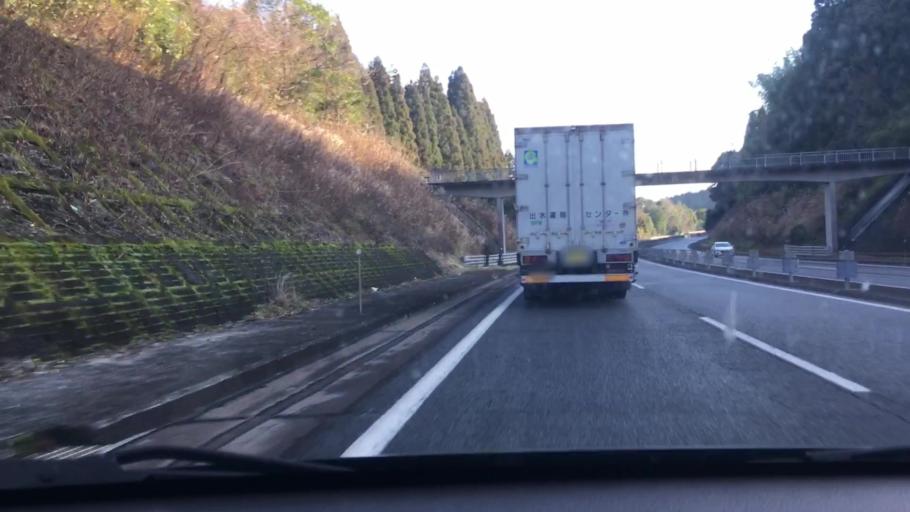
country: JP
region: Kagoshima
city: Okuchi-shinohara
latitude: 31.9093
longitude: 130.7063
